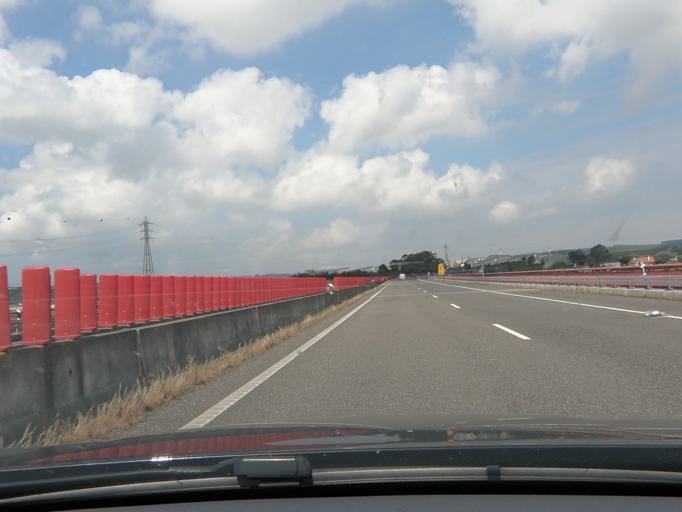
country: PT
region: Leiria
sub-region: Obidos
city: Obidos
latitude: 39.3339
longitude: -9.1998
